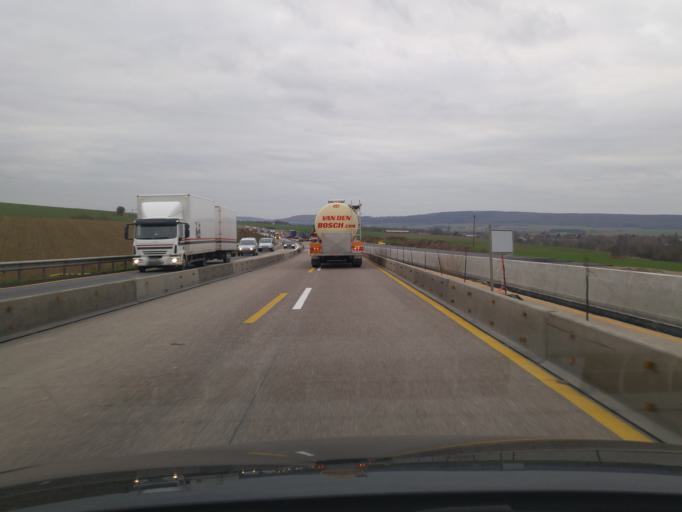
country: DE
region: Lower Saxony
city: Bockenem
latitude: 51.9625
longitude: 10.1409
